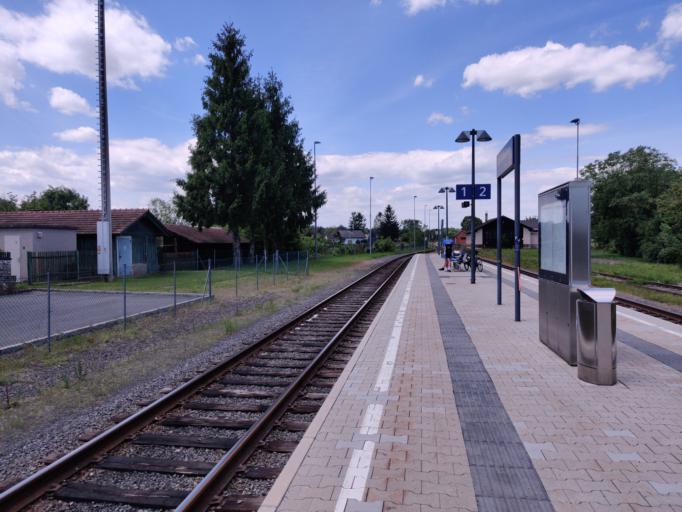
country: AT
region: Styria
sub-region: Politischer Bezirk Suedoststeiermark
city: Bad Radkersburg
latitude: 46.6995
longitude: 15.9933
